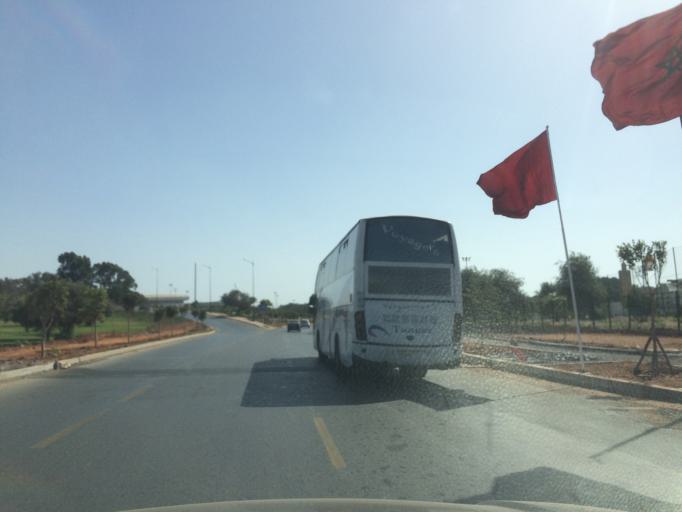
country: MA
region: Rabat-Sale-Zemmour-Zaer
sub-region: Skhirate-Temara
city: Temara
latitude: 33.9700
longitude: -6.8825
